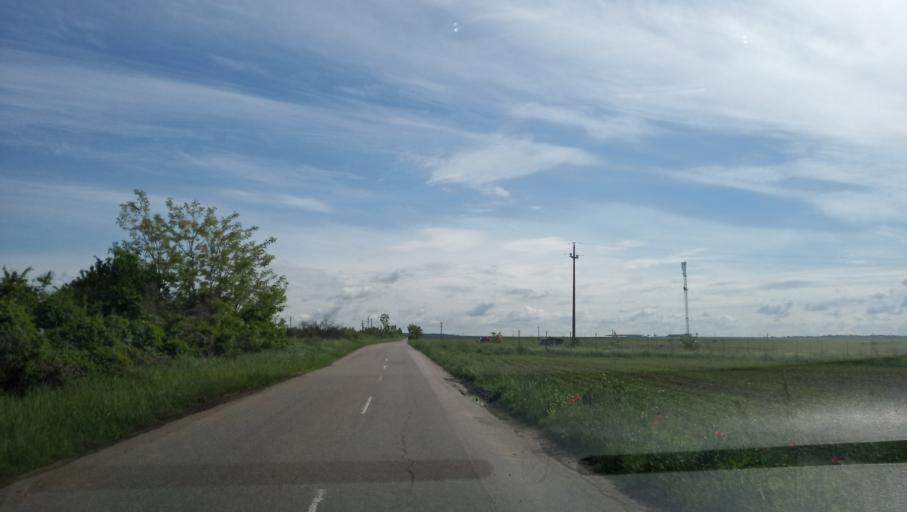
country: RO
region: Timis
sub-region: Comuna Topolovatu Mare
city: Topolovatu Mare
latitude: 45.7762
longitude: 21.6312
